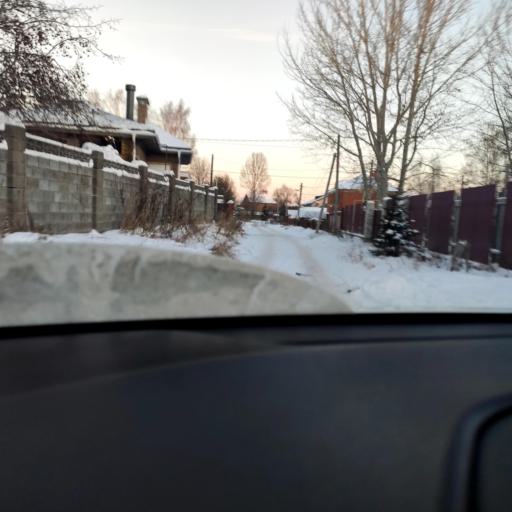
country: RU
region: Tatarstan
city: Stolbishchi
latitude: 55.7477
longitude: 49.2529
